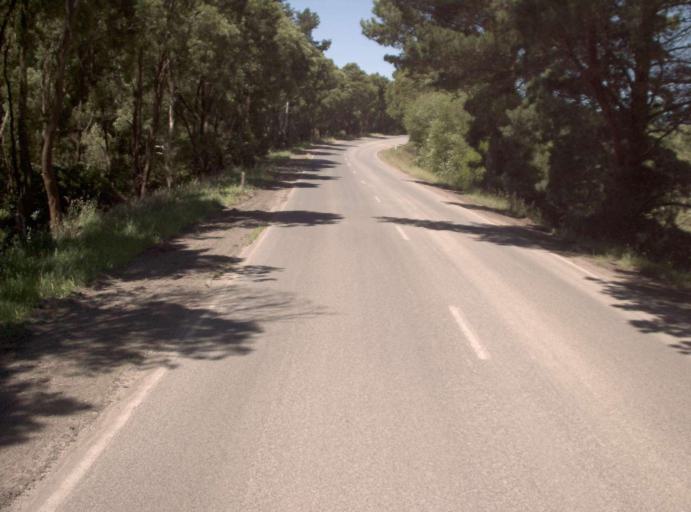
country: AU
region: Victoria
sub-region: Bass Coast
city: North Wonthaggi
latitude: -38.6955
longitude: 146.0956
